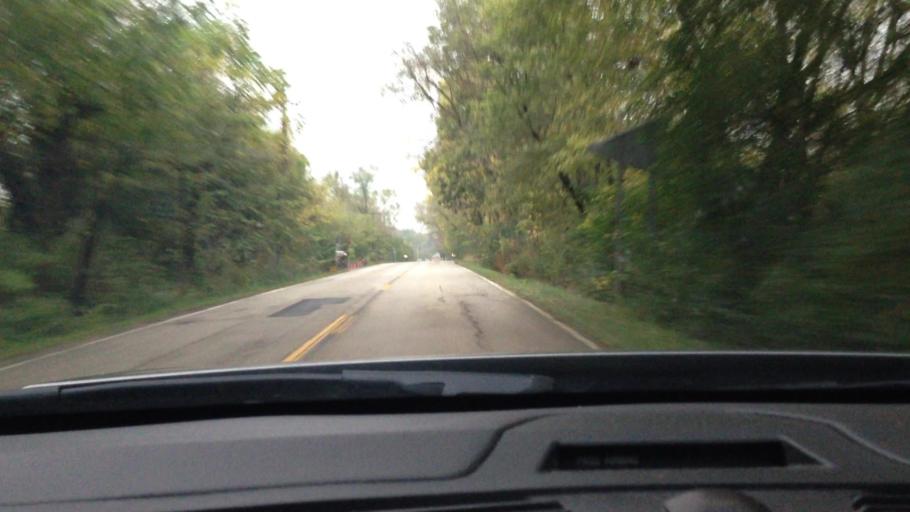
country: US
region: Illinois
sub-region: Cook County
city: Barrington Hills
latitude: 42.0993
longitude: -88.1947
